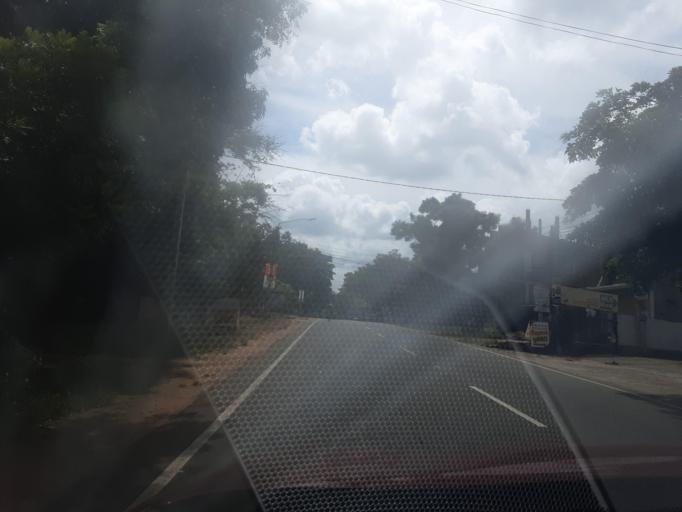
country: LK
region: North Western
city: Kuliyapitiya
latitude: 7.4694
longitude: 80.0532
